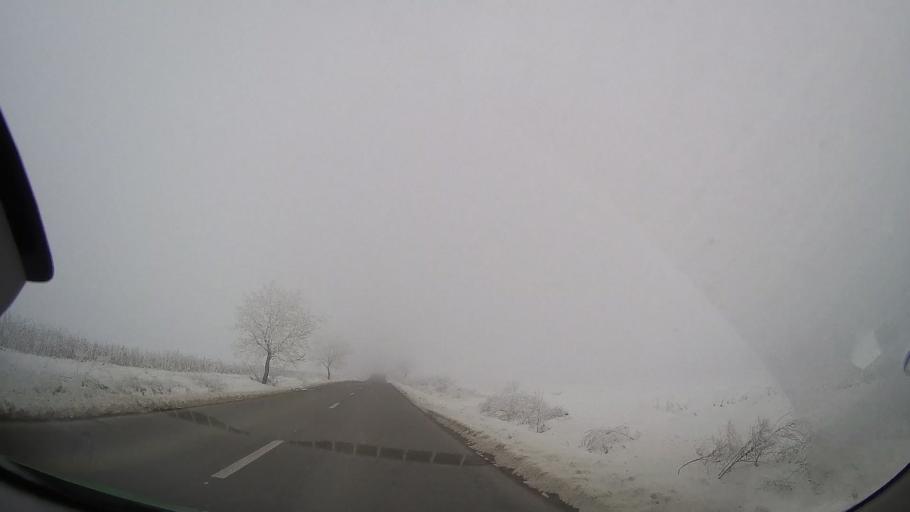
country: RO
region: Iasi
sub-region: Comuna Mogosesti-Siret
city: Mogosesti-Siret
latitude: 47.1516
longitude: 26.7774
